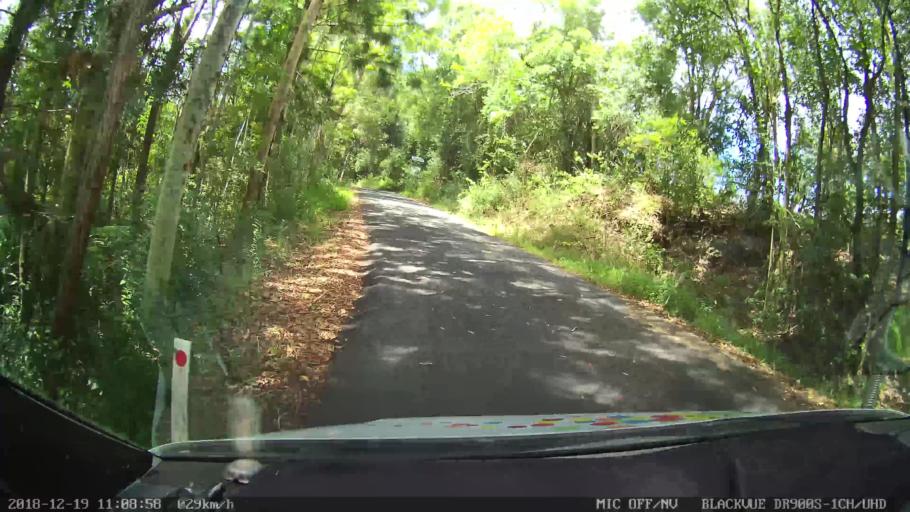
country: AU
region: New South Wales
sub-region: Lismore Municipality
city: Nimbin
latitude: -28.6322
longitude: 153.2641
